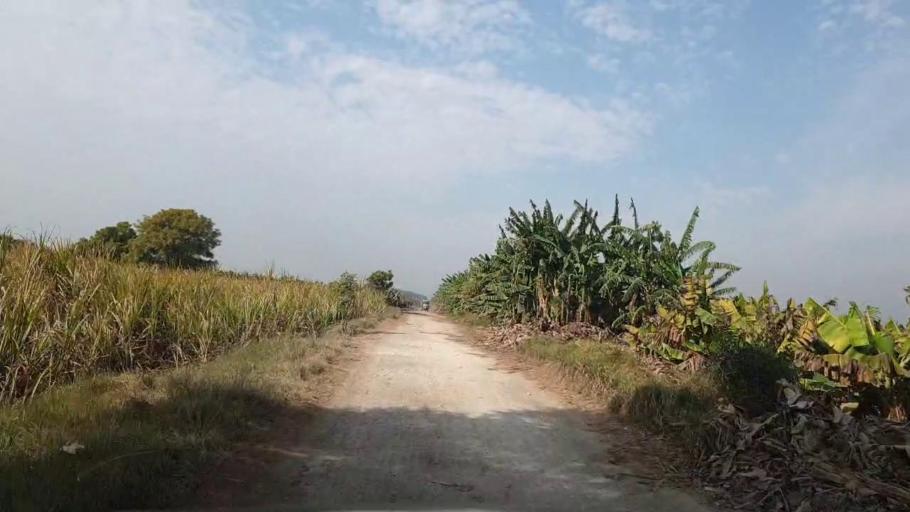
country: PK
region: Sindh
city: Matiari
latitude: 25.5575
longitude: 68.5187
